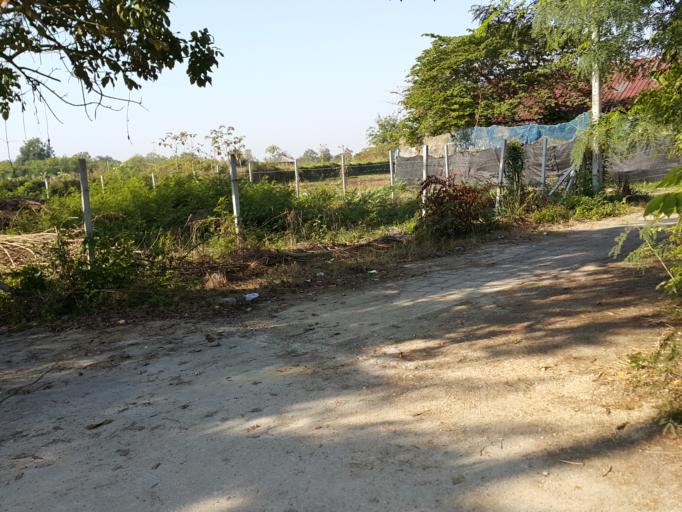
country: TH
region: Chiang Mai
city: San Kamphaeng
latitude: 18.8046
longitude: 99.1092
